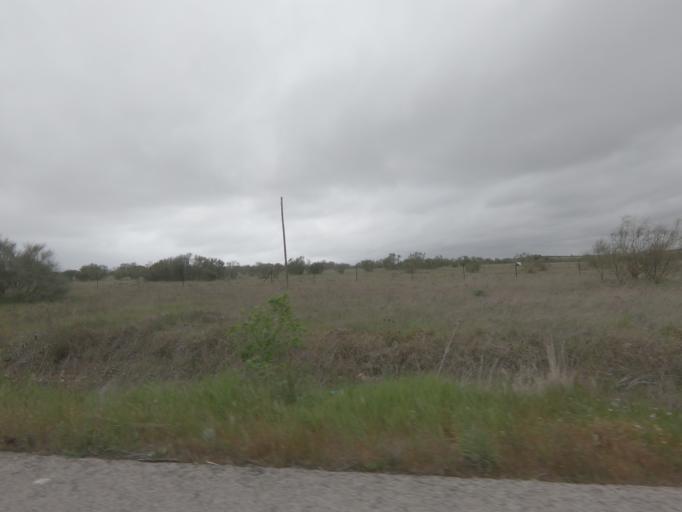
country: ES
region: Extremadura
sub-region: Provincia de Caceres
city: Malpartida de Caceres
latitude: 39.3704
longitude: -6.4559
